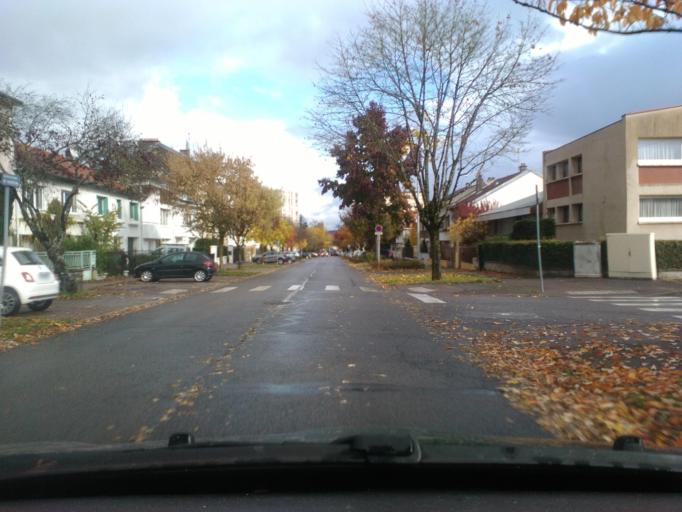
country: FR
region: Lorraine
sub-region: Departement de Meurthe-et-Moselle
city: Laxou
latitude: 48.6784
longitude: 6.1505
